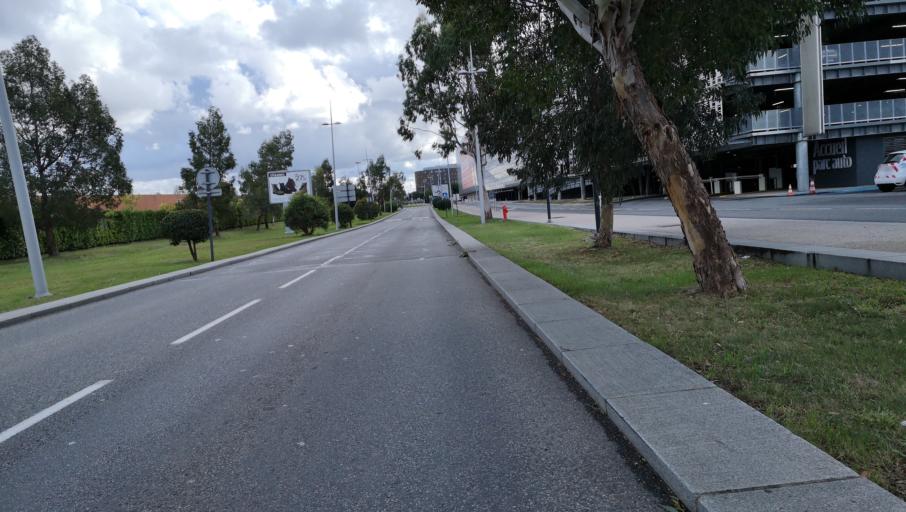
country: FR
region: Midi-Pyrenees
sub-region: Departement de la Haute-Garonne
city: Blagnac
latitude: 43.6342
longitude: 1.3729
